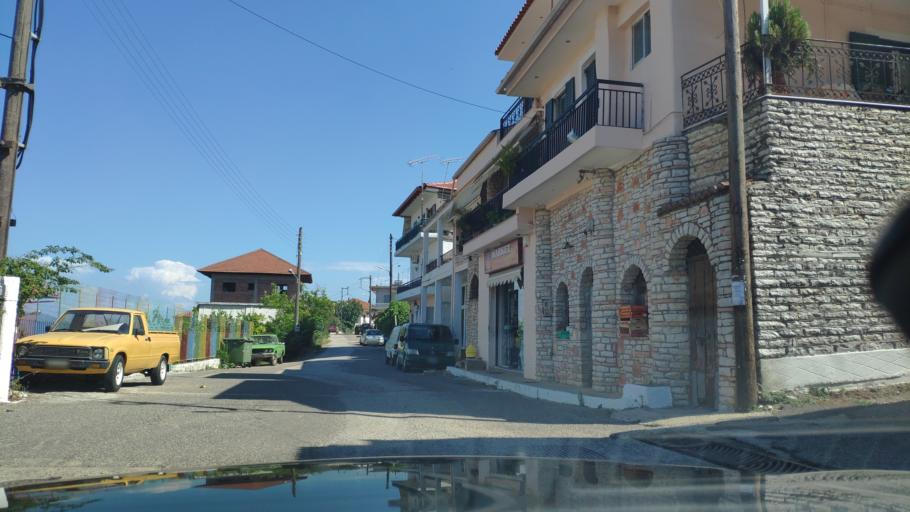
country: GR
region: West Greece
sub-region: Nomos Aitolias kai Akarnanias
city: Katouna
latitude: 38.7890
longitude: 21.1150
